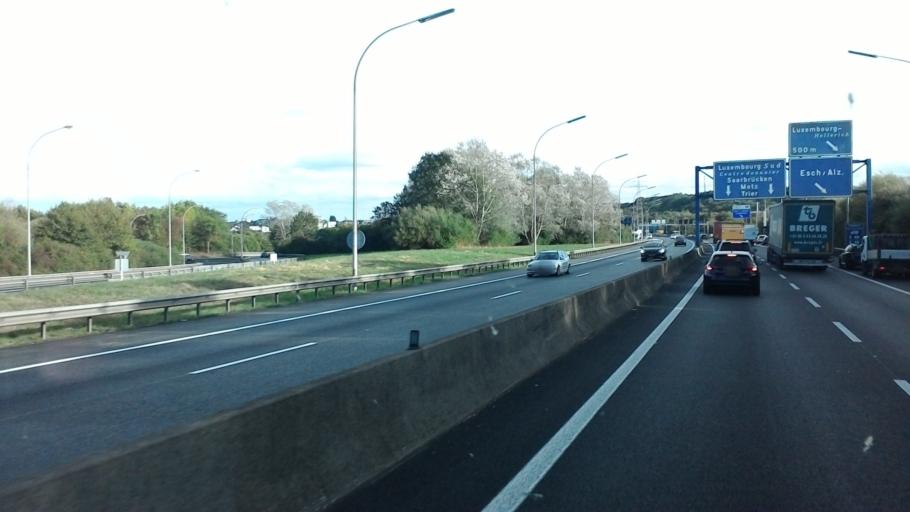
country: LU
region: Luxembourg
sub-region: Canton d'Esch-sur-Alzette
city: Leudelange
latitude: 49.5891
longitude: 6.0839
